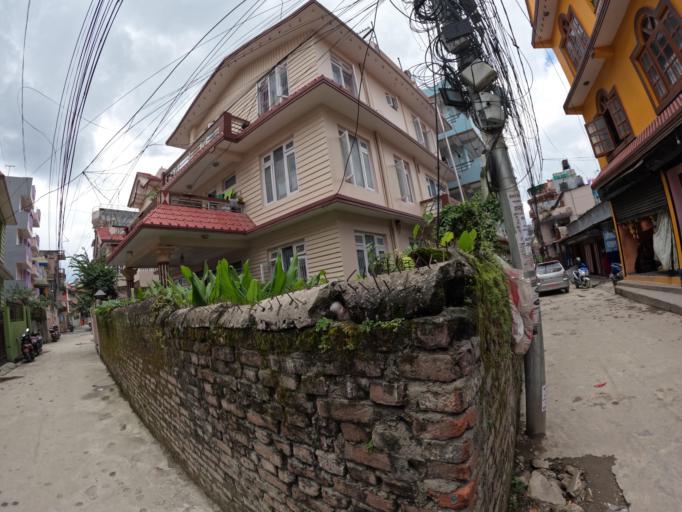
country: NP
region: Central Region
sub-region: Bagmati Zone
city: Kathmandu
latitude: 27.7399
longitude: 85.3128
